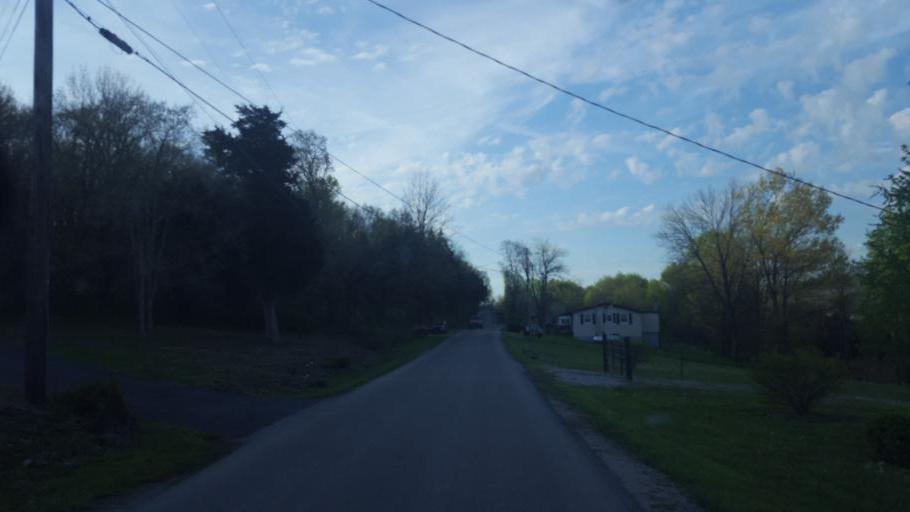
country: US
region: Kentucky
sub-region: Hart County
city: Munfordville
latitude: 37.2445
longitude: -85.8990
